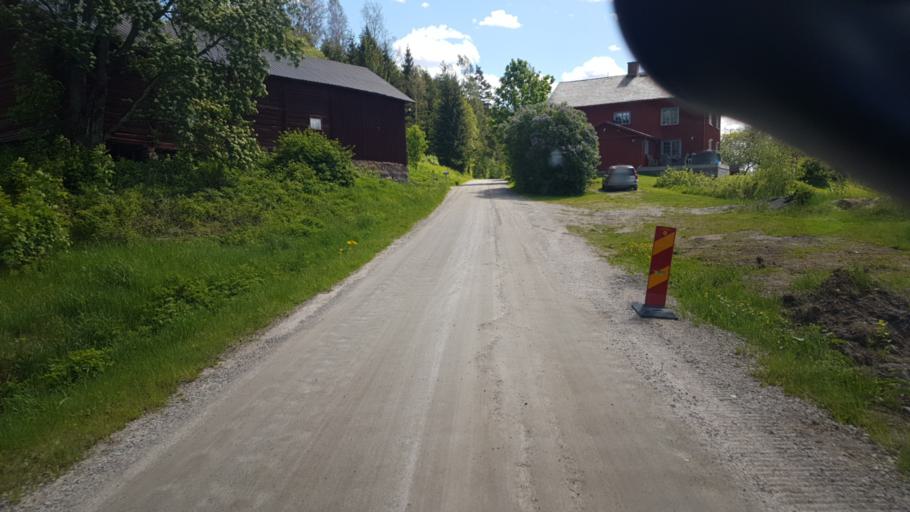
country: SE
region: Vaermland
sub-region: Arvika Kommun
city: Arvika
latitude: 59.7349
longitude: 12.8316
